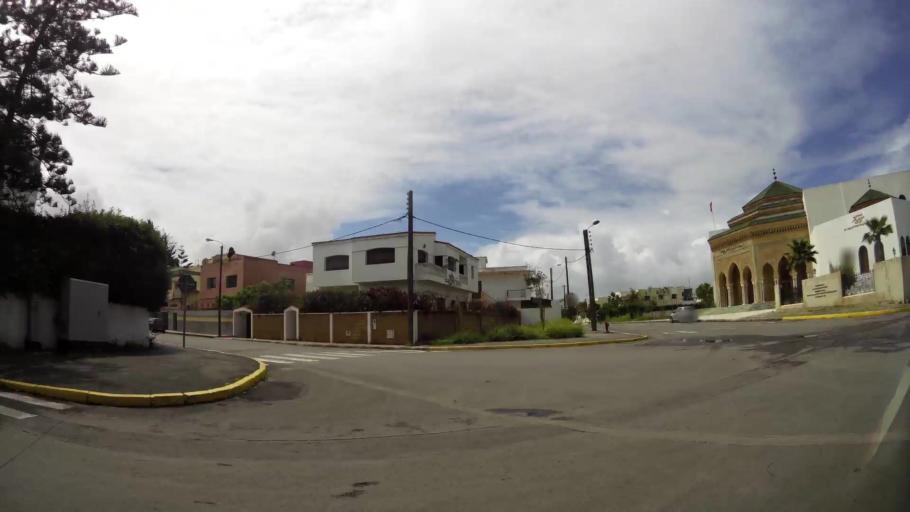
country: MA
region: Grand Casablanca
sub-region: Casablanca
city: Casablanca
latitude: 33.5662
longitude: -7.6345
